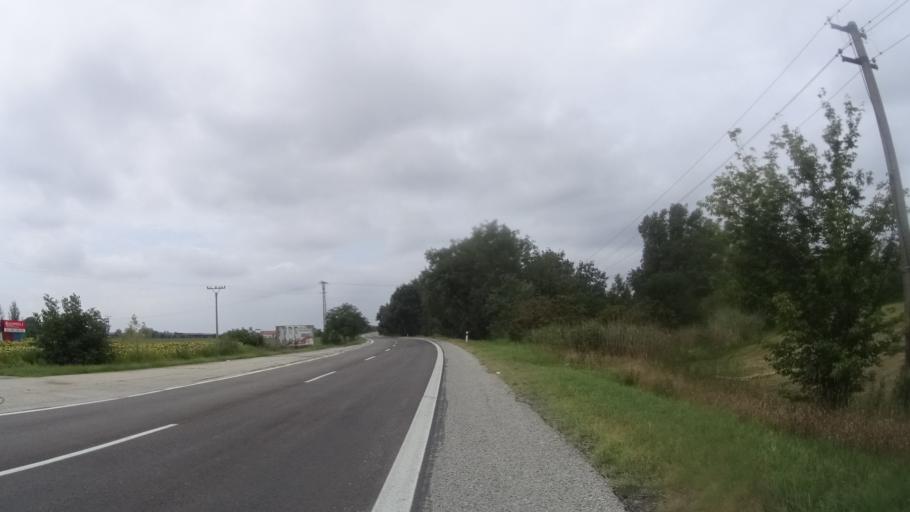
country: HU
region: Komarom-Esztergom
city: Acs
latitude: 47.7662
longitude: 18.0338
